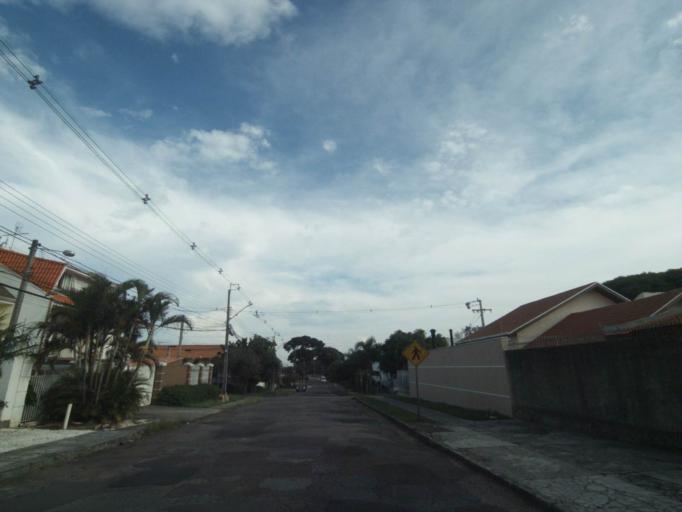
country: BR
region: Parana
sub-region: Pinhais
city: Pinhais
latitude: -25.4536
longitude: -49.2245
